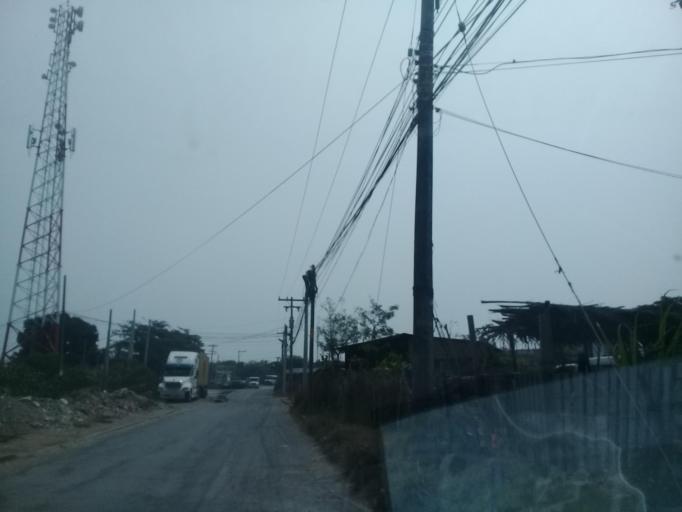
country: MX
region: Veracruz
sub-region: Veracruz
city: Fraccionamiento Costa Dorada
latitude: 19.2114
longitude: -96.2192
